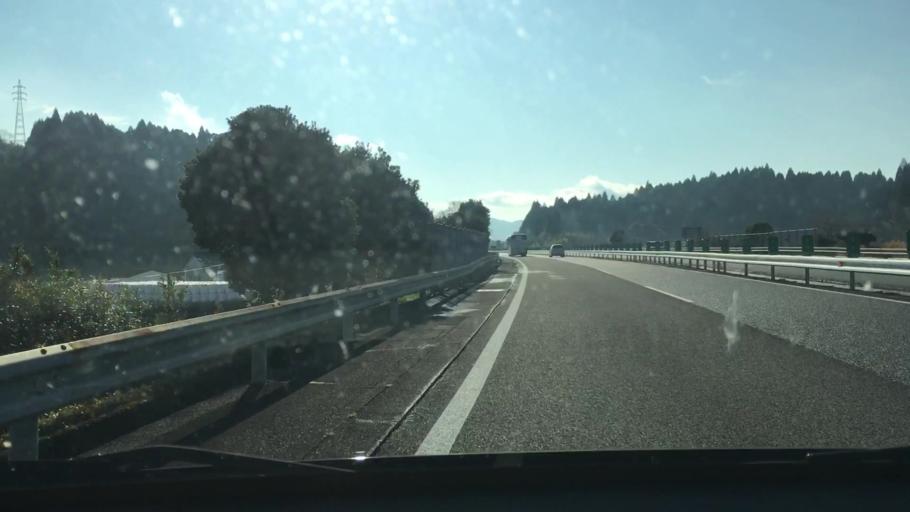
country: JP
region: Kagoshima
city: Okuchi-shinohara
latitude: 32.0215
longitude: 130.7750
